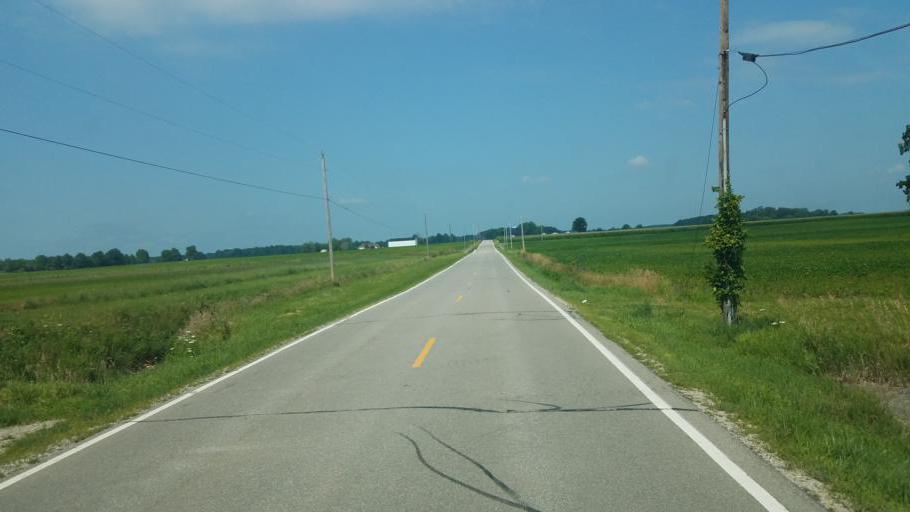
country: US
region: Ohio
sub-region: Crawford County
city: Galion
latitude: 40.7561
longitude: -82.8434
